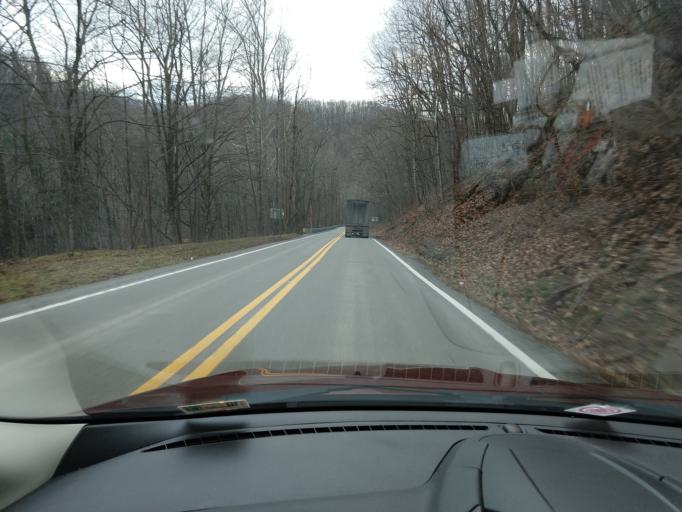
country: US
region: West Virginia
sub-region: Randolph County
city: Elkins
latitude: 38.6616
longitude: -79.9287
